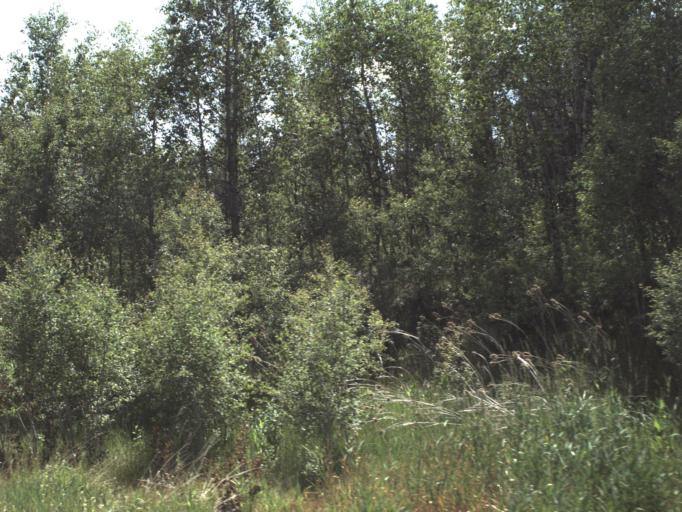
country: US
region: Utah
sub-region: Weber County
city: Wolf Creek
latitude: 41.3083
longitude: -111.6164
